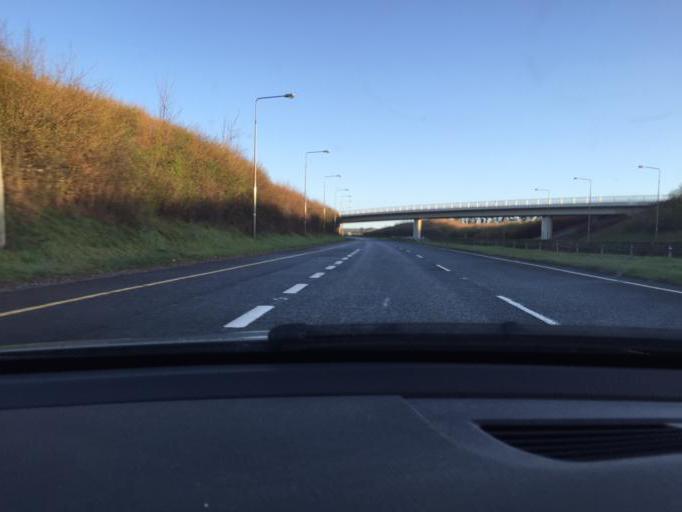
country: IE
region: Leinster
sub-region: Lu
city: Tullyallen
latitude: 53.7333
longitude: -6.3972
